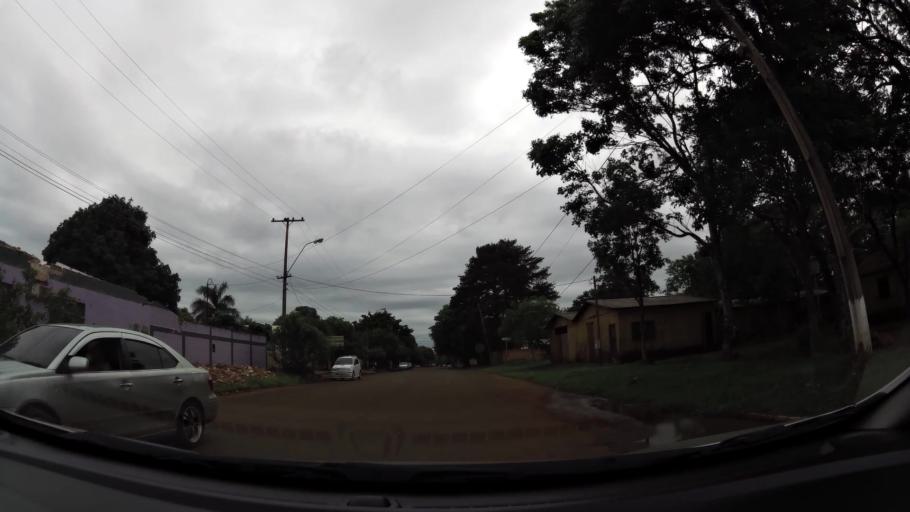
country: PY
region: Alto Parana
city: Ciudad del Este
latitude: -25.4042
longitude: -54.6450
